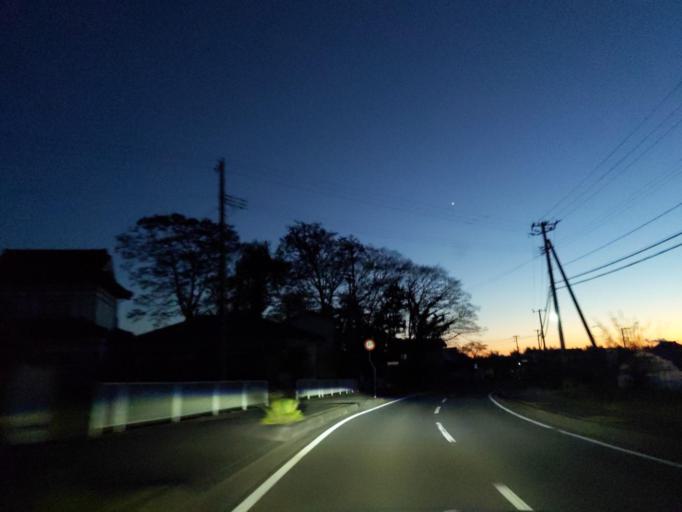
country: JP
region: Fukushima
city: Sukagawa
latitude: 37.3105
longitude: 140.3822
